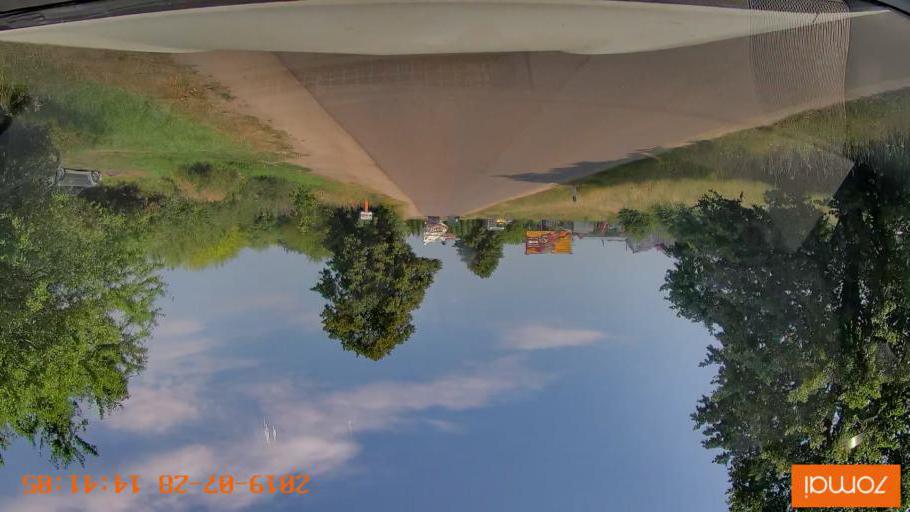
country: RU
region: Kaliningrad
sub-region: Gorod Kaliningrad
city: Yantarnyy
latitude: 54.8549
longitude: 19.9510
